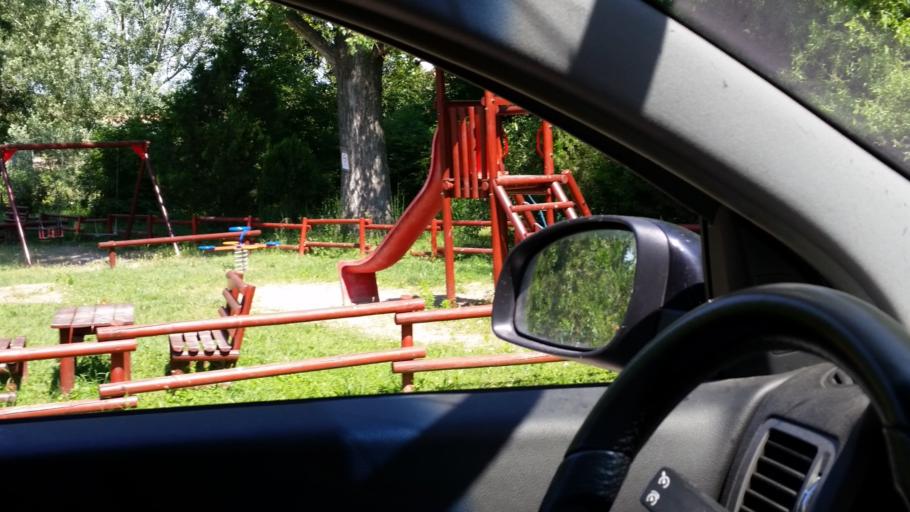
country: HU
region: Fejer
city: Many
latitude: 47.5546
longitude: 18.5959
